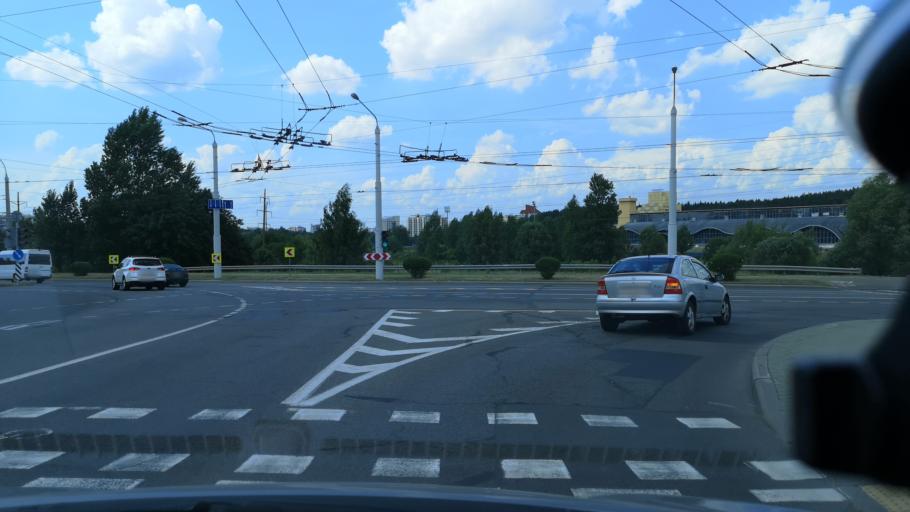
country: BY
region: Minsk
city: Borovlyany
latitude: 53.9420
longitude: 27.6522
